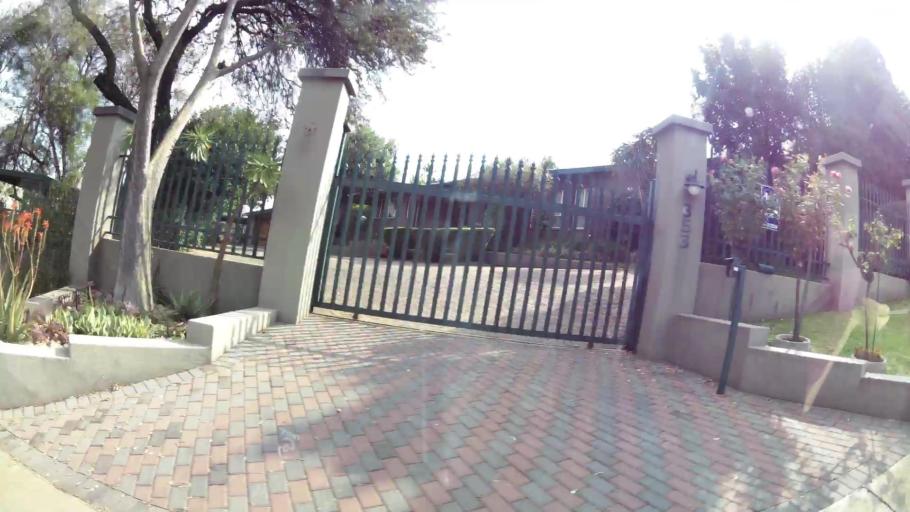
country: ZA
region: Gauteng
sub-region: City of Tshwane Metropolitan Municipality
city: Pretoria
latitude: -25.7743
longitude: 28.3033
